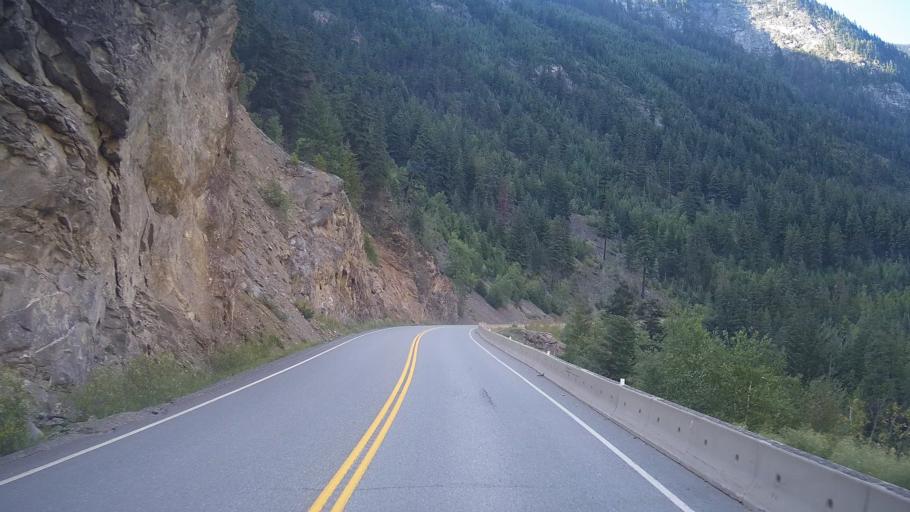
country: CA
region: British Columbia
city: Lillooet
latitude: 50.6448
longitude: -122.0696
